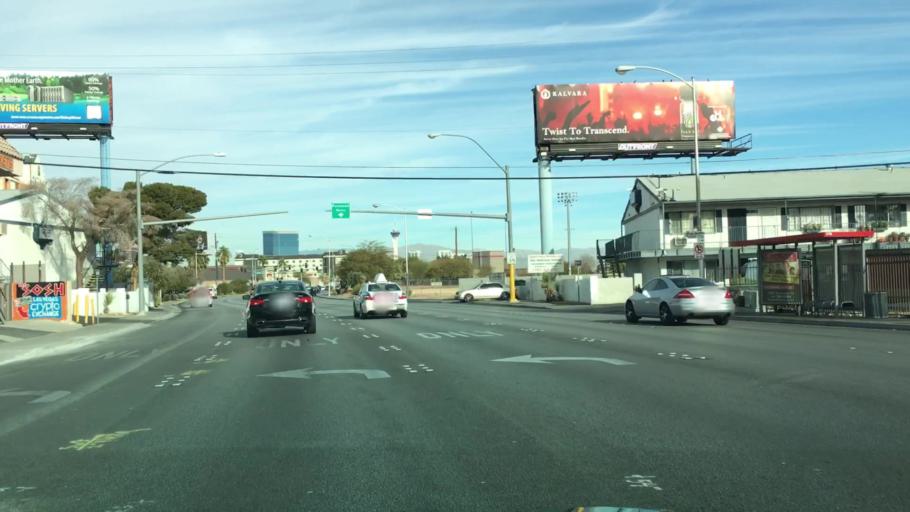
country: US
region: Nevada
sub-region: Clark County
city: Paradise
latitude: 36.1058
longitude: -115.1499
